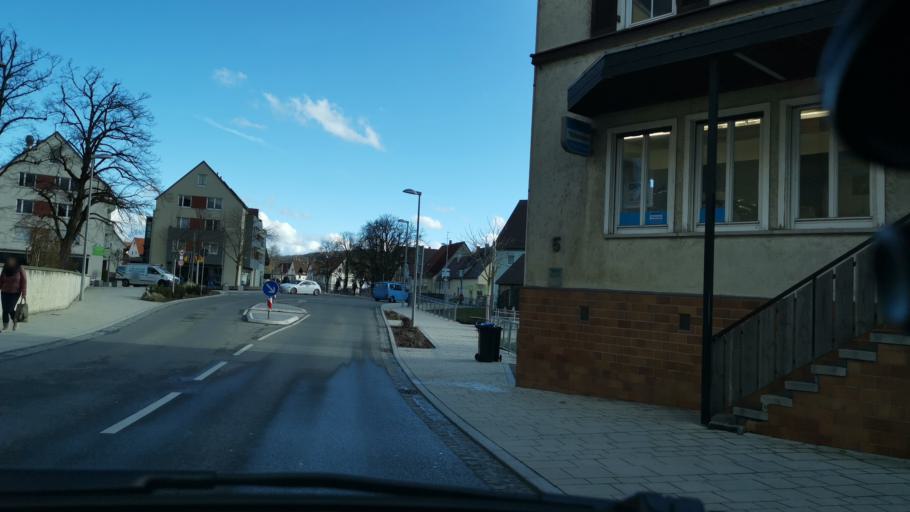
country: DE
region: Baden-Wuerttemberg
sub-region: Regierungsbezirk Stuttgart
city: Renningen
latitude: 48.7752
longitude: 8.9027
